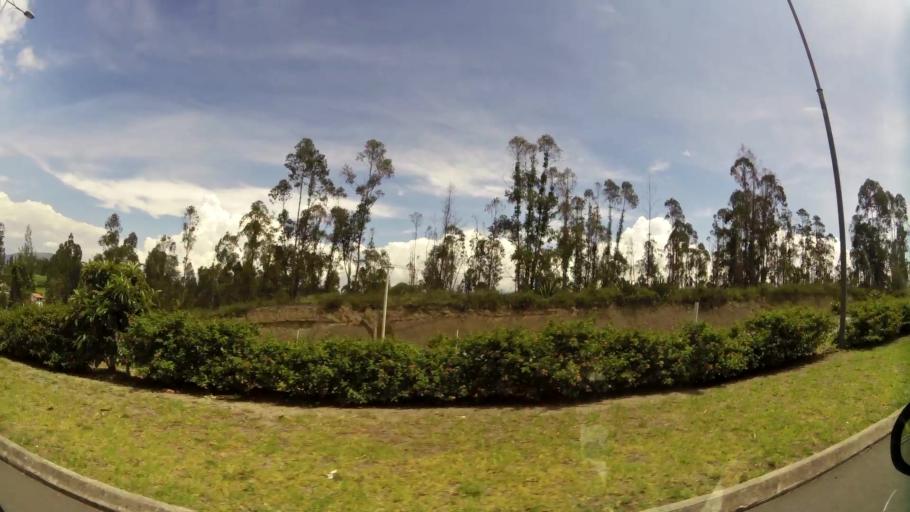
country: EC
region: Pichincha
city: Quito
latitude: -0.1702
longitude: -78.3432
